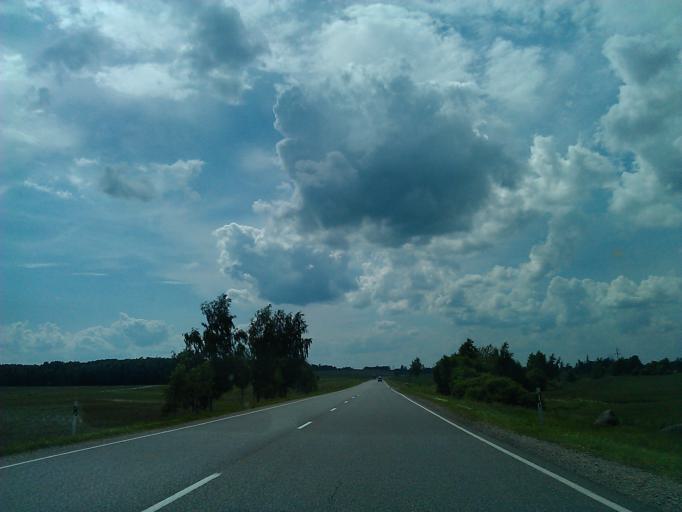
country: LV
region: Jaunpils
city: Jaunpils
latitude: 56.6636
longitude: 23.0228
